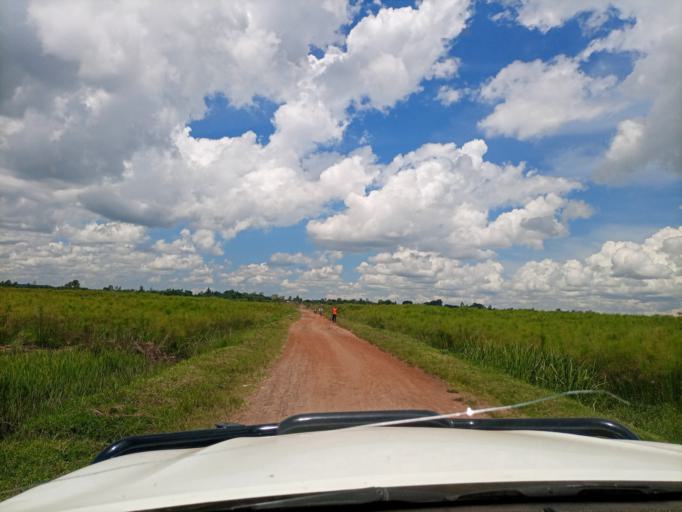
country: UG
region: Eastern Region
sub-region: Tororo District
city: Tororo
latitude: 0.6390
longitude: 33.9936
